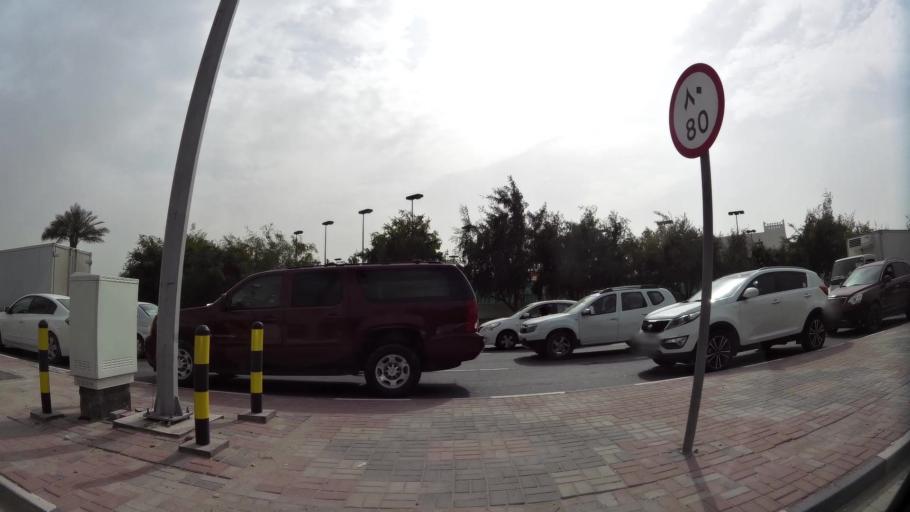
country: QA
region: Baladiyat ad Dawhah
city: Doha
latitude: 25.3141
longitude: 51.5165
